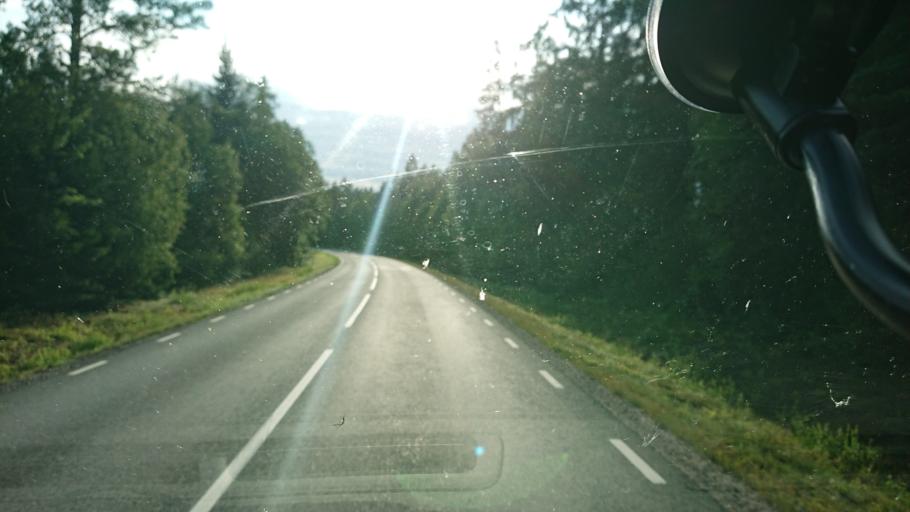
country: SE
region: Kronoberg
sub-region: Vaxjo Kommun
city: Rottne
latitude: 57.0373
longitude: 14.9181
